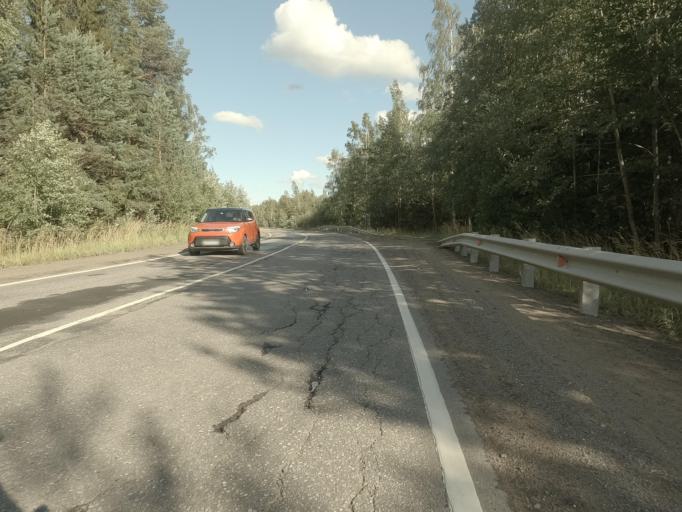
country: RU
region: Leningrad
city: Borisova Griva
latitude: 59.9853
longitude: 30.8914
